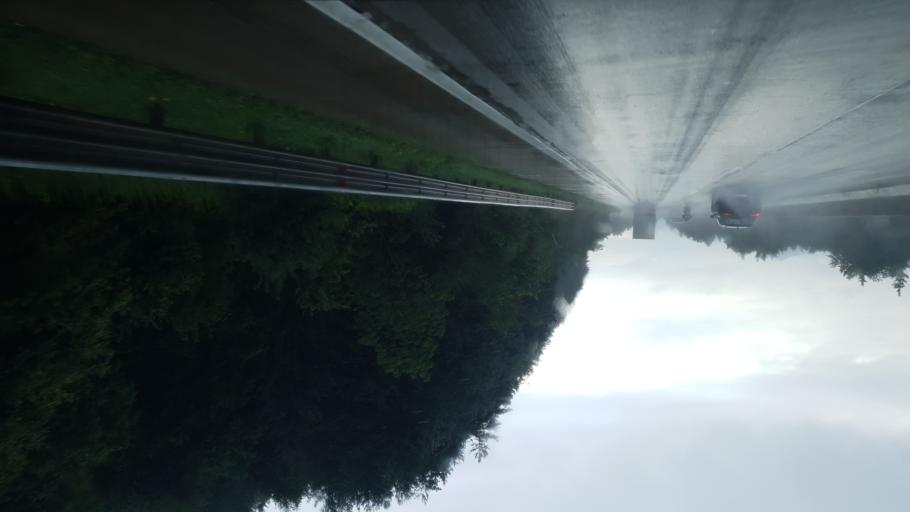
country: AT
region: Carinthia
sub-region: Politischer Bezirk Spittal an der Drau
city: Spittal an der Drau
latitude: 46.7874
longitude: 13.5299
